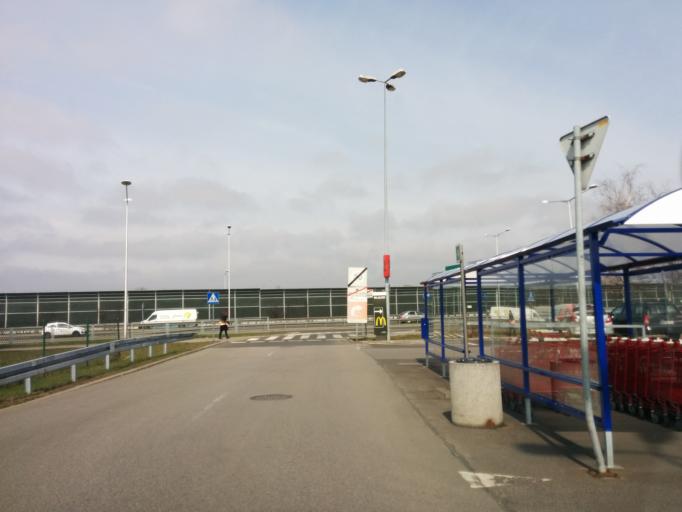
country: PL
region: Masovian Voivodeship
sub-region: Warszawa
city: Targowek
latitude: 52.3050
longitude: 21.0562
